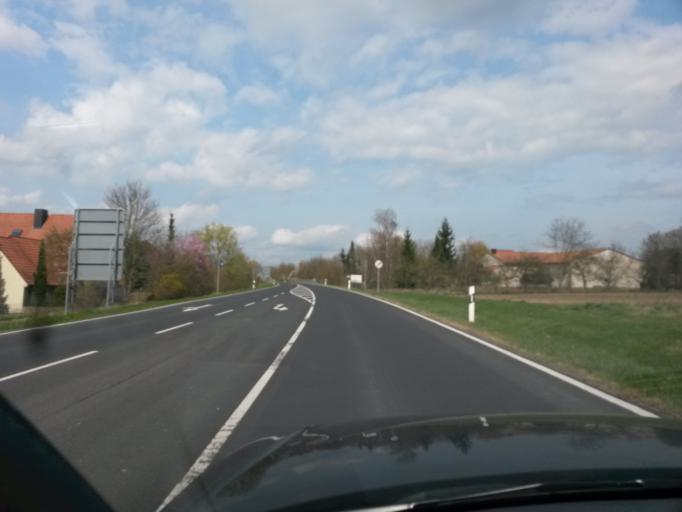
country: DE
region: Bavaria
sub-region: Regierungsbezirk Unterfranken
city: Volkach
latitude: 49.8604
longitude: 10.2420
